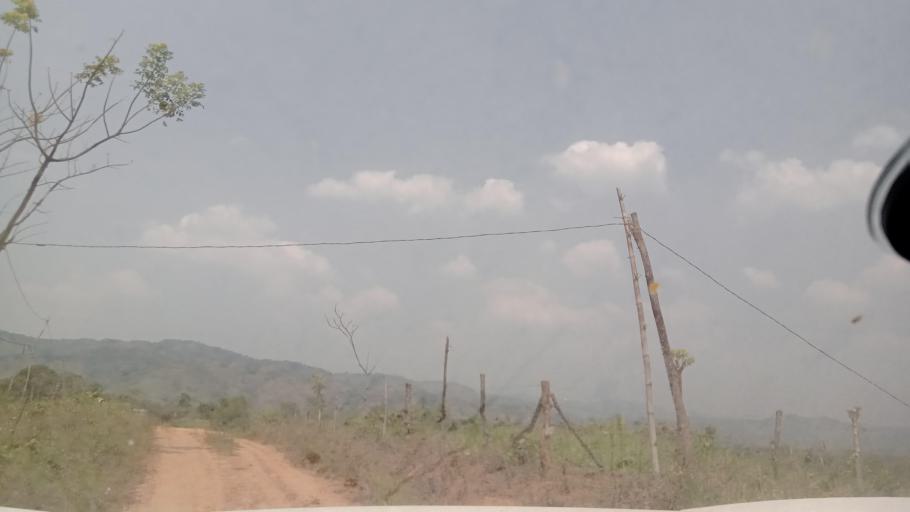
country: MX
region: Chiapas
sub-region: Tecpatan
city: Raudales Malpaso
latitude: 17.4674
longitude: -93.8267
